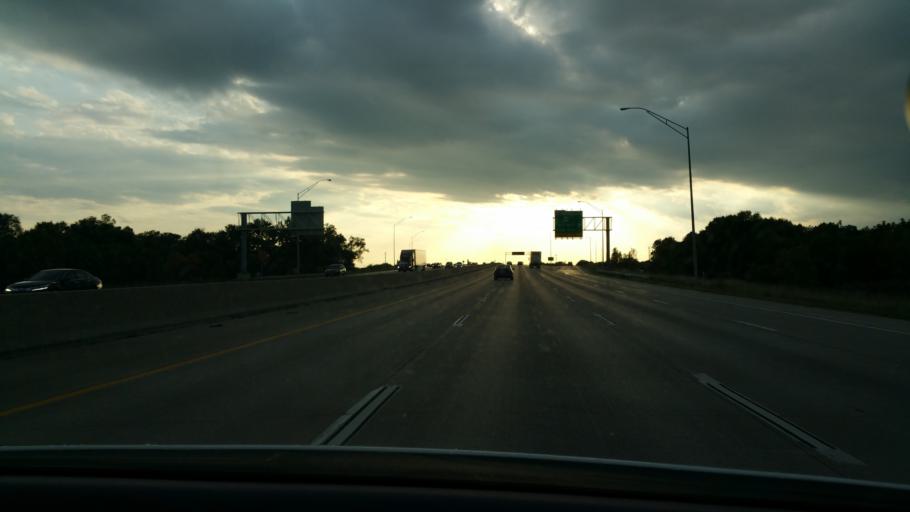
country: US
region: Iowa
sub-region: Polk County
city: Saylorville
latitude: 41.6496
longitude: -93.6108
